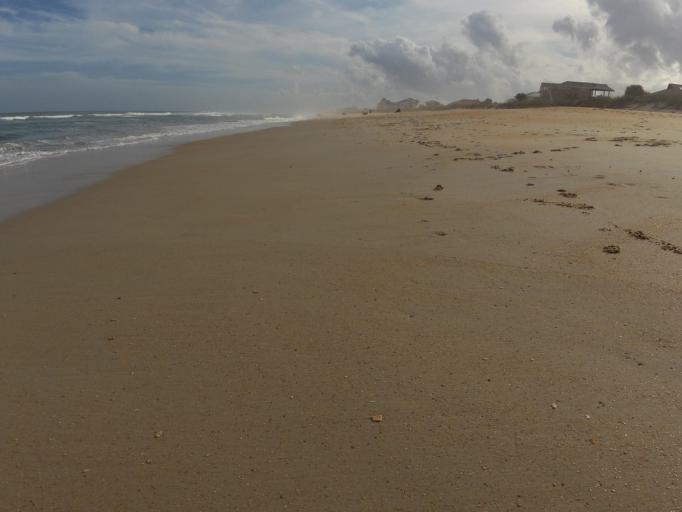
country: US
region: Florida
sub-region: Flagler County
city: Palm Coast
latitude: 29.6325
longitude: -81.1971
